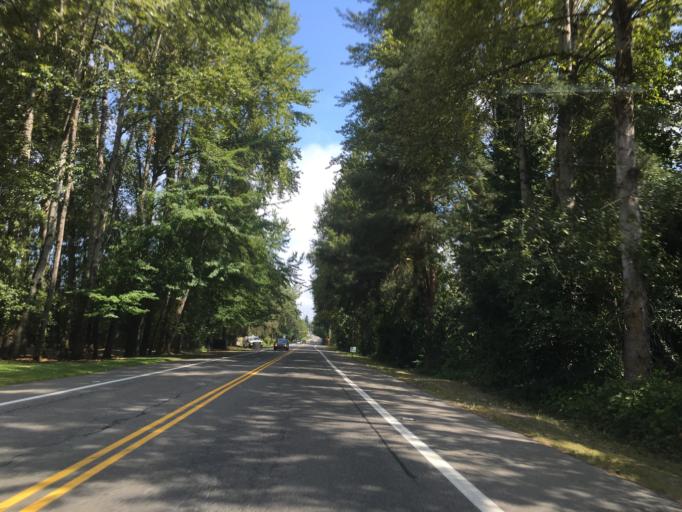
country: US
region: Washington
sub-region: King County
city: Kingsgate
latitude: 47.7349
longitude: -122.1937
